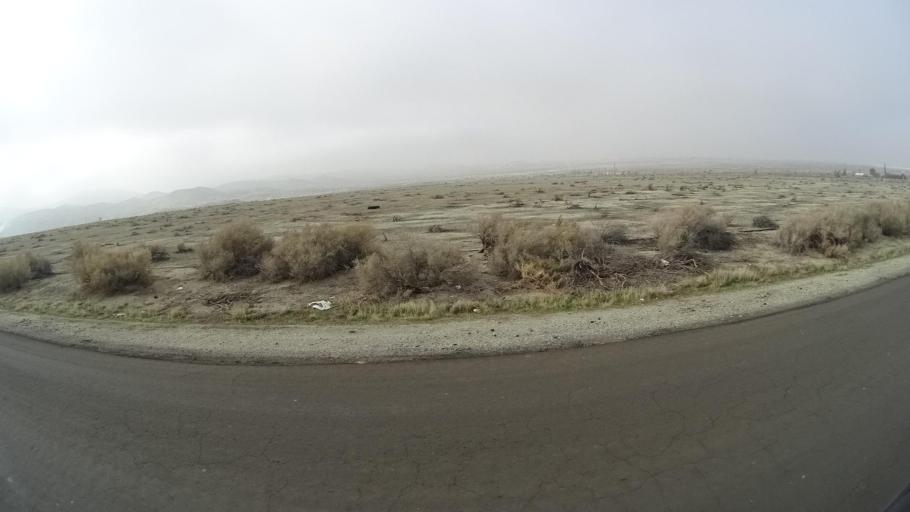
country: US
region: California
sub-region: Kern County
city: Maricopa
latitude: 35.0424
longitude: -119.3670
